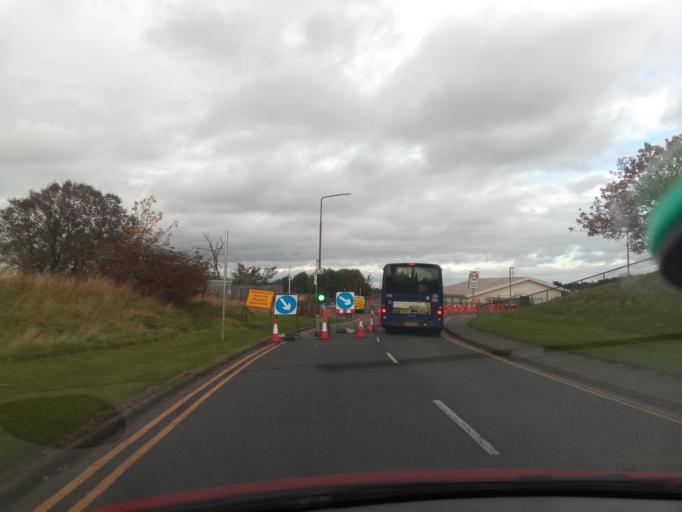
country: GB
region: Scotland
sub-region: West Lothian
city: Blackburn
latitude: 55.8439
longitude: -3.6180
